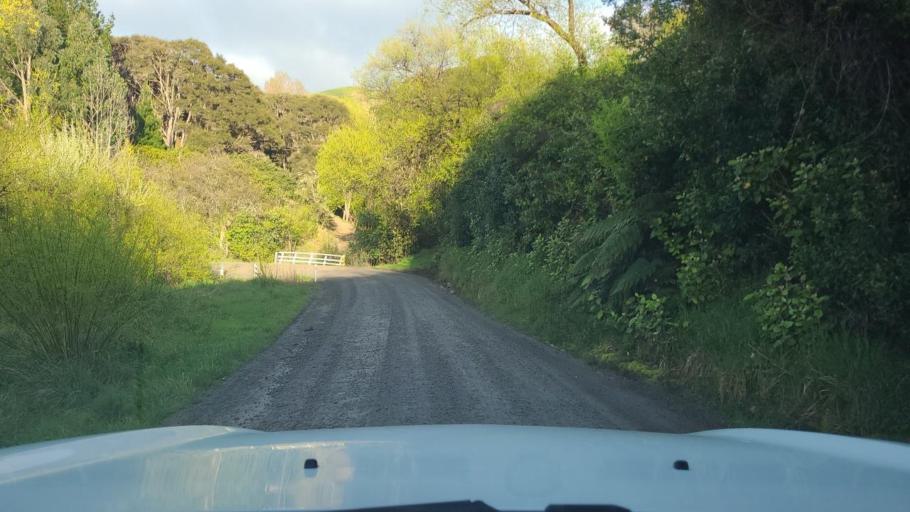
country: NZ
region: Wellington
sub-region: Masterton District
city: Masterton
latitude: -41.1879
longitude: 175.6725
